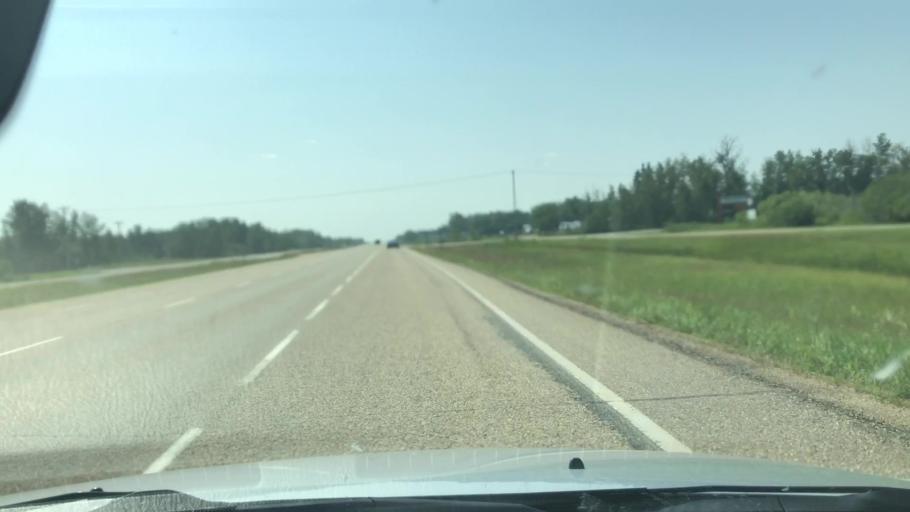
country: CA
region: Alberta
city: Devon
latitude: 53.4259
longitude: -113.7638
